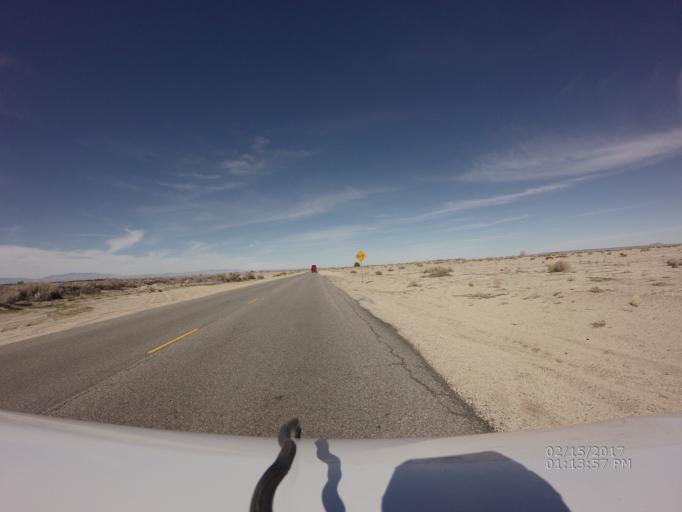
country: US
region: California
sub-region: Los Angeles County
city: Littlerock
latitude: 34.6181
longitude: -118.0053
